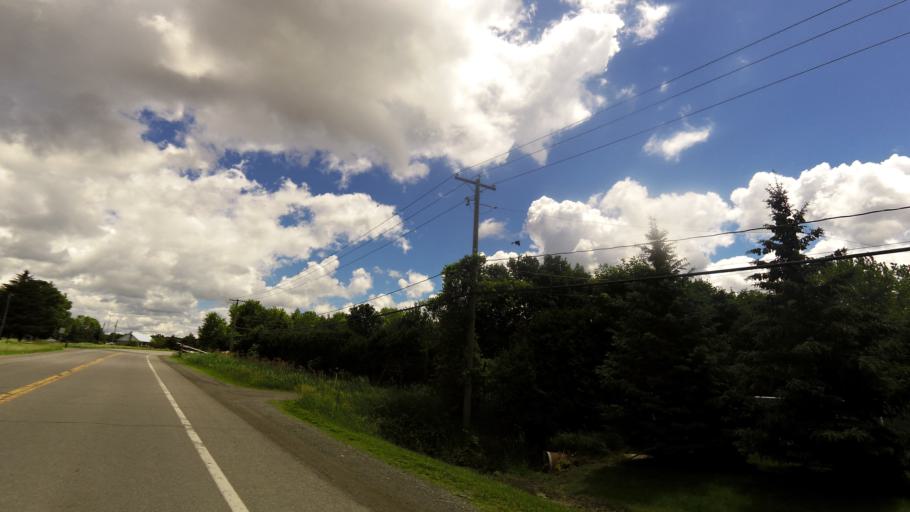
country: CA
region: Quebec
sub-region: Monteregie
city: Hudson
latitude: 45.5303
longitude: -74.1858
